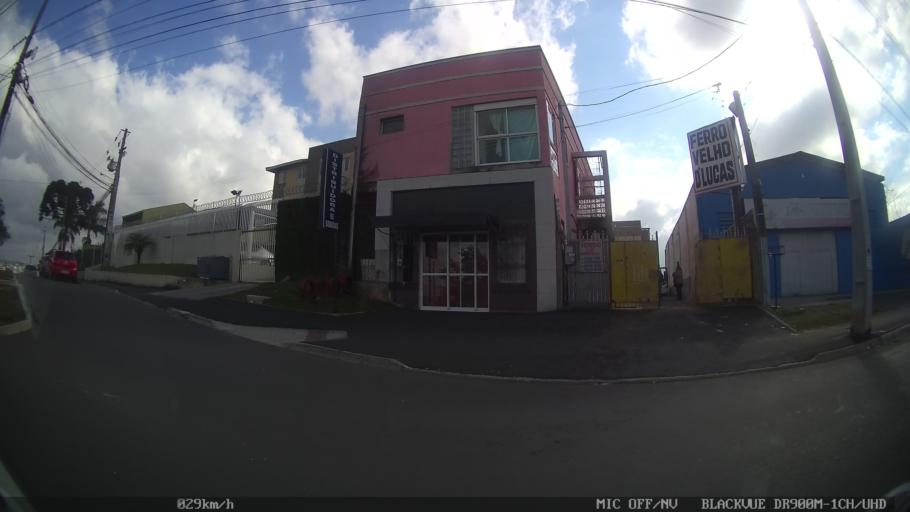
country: BR
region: Parana
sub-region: Pinhais
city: Pinhais
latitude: -25.3701
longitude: -49.1863
